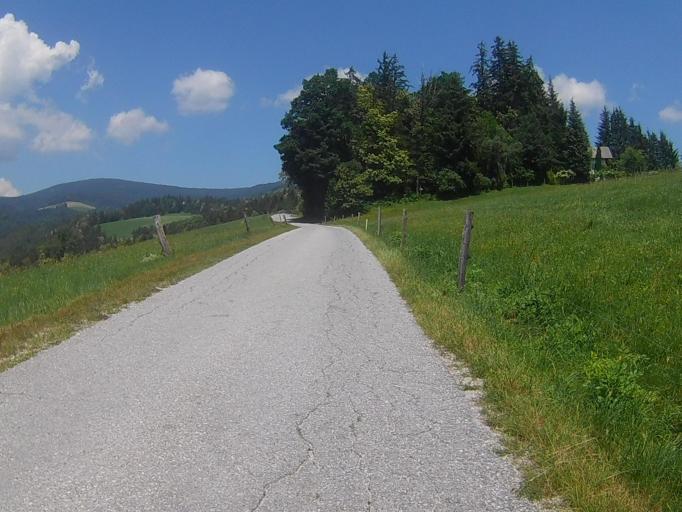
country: SI
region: Race-Fram
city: Morje
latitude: 46.4774
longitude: 15.5877
